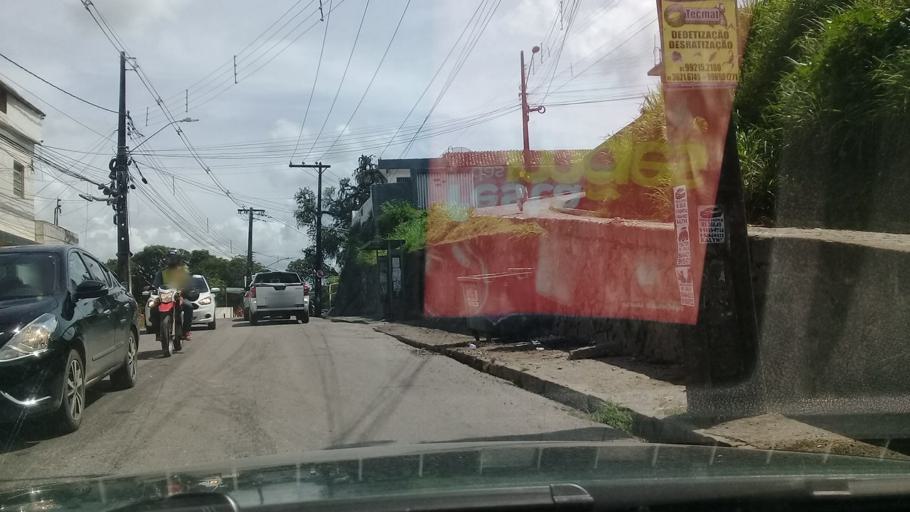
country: BR
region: Pernambuco
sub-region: Jaboatao Dos Guararapes
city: Jaboatao dos Guararapes
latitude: -8.1073
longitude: -35.0172
